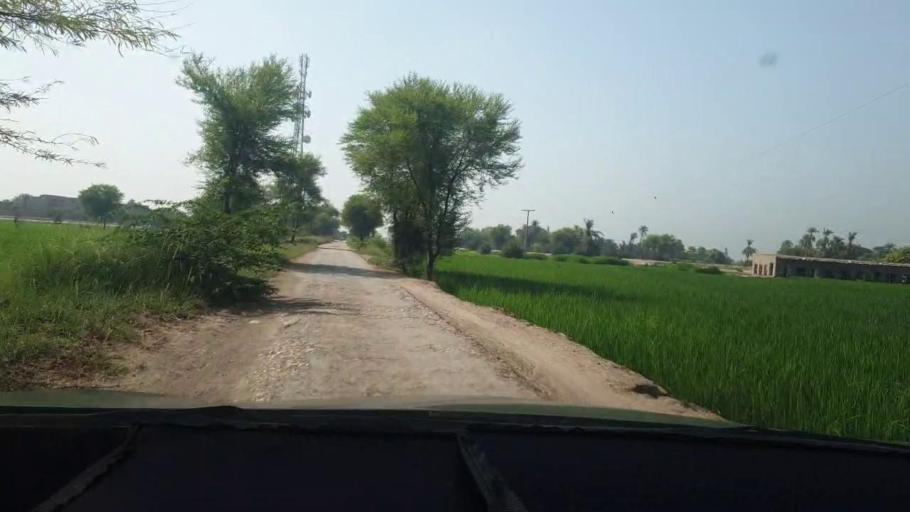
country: PK
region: Sindh
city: Kambar
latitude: 27.5611
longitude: 68.0587
